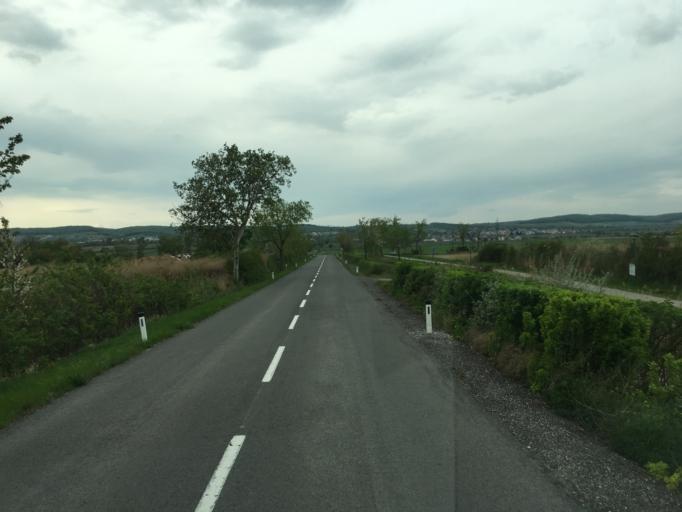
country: AT
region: Burgenland
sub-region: Politischer Bezirk Neusiedl am See
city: Winden am See
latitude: 47.9302
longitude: 16.7485
